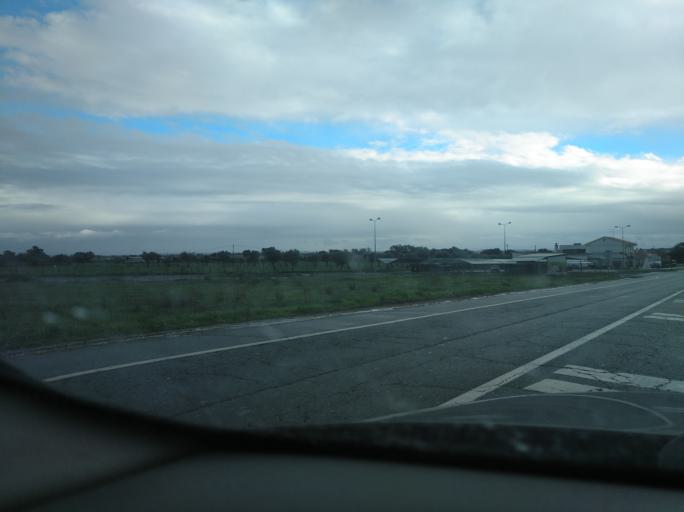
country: PT
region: Beja
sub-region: Aljustrel
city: Aljustrel
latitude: 37.9506
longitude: -8.3809
